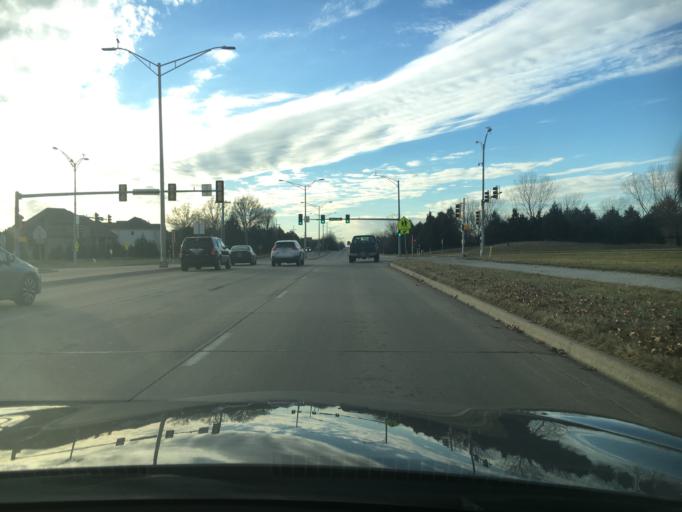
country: US
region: Kansas
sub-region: Johnson County
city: Leawood
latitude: 38.8693
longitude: -94.6484
